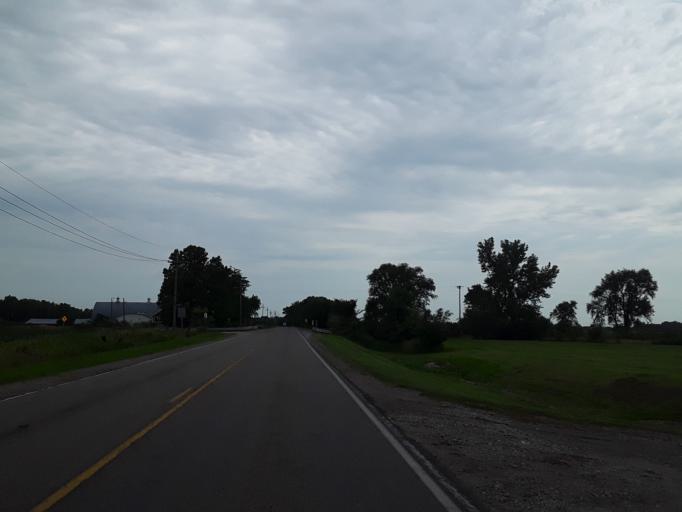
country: US
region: Nebraska
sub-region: Saunders County
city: Yutan
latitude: 41.2207
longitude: -96.3303
